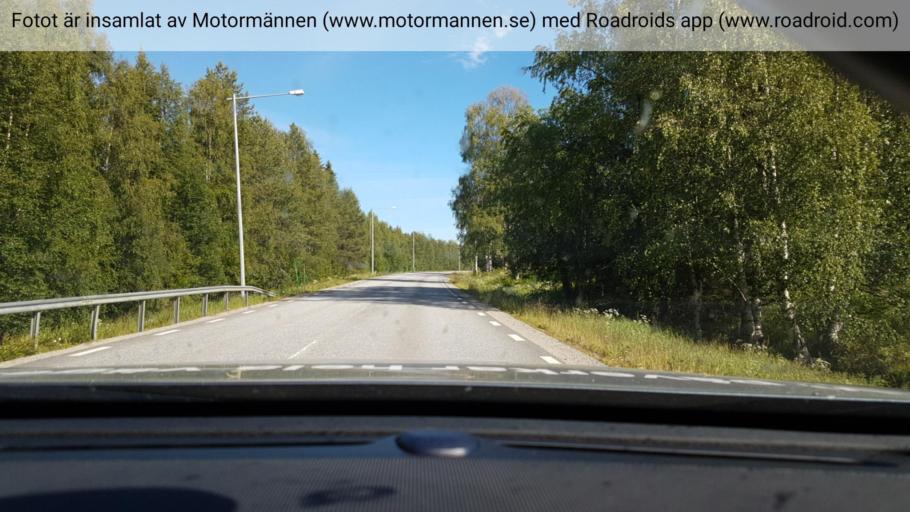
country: SE
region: Vaesterbotten
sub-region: Lycksele Kommun
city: Lycksele
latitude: 64.6938
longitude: 18.3937
